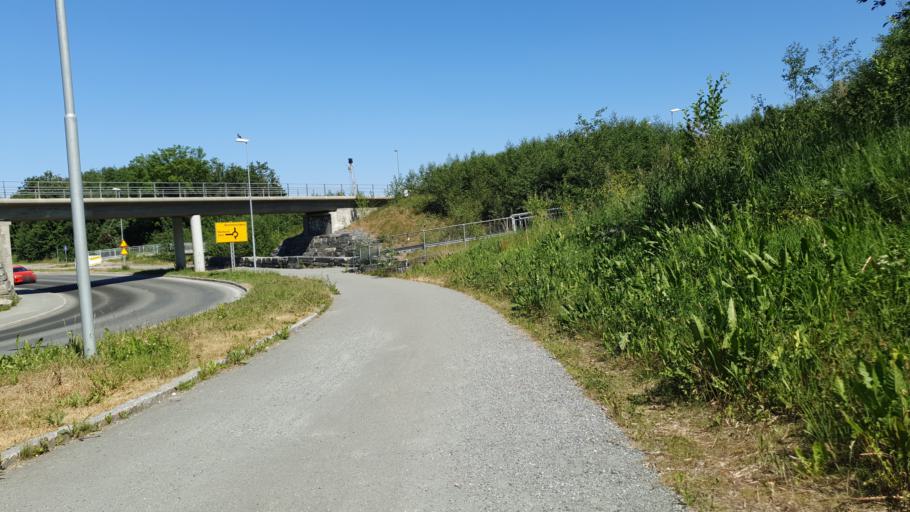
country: NO
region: Sor-Trondelag
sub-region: Trondheim
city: Trondheim
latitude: 63.4265
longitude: 10.5308
